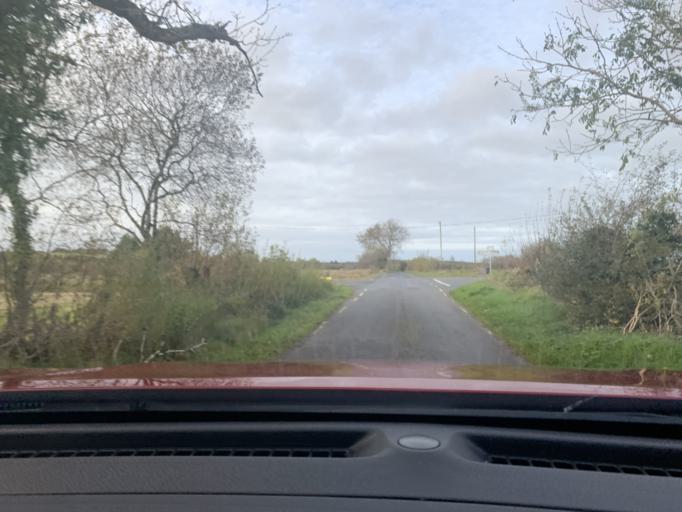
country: IE
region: Connaught
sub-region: Roscommon
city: Ballaghaderreen
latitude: 54.0004
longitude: -8.6069
